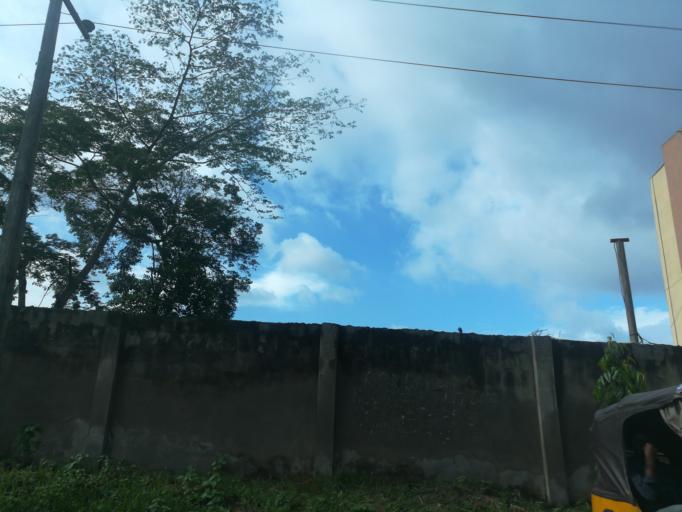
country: NG
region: Lagos
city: Ikeja
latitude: 6.6203
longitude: 3.3571
